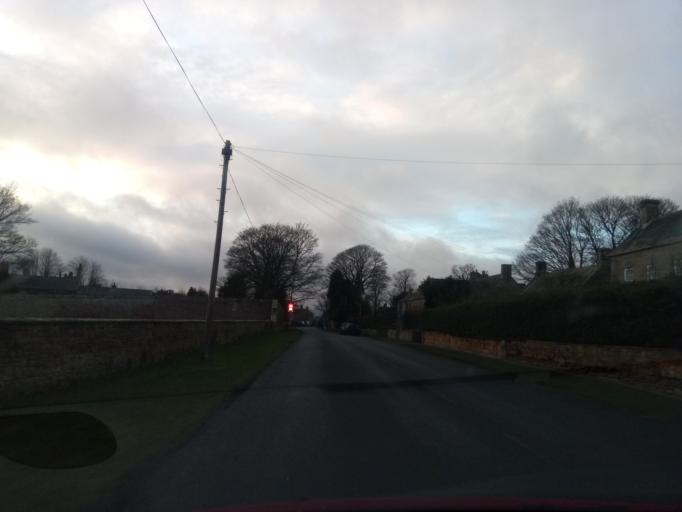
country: GB
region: England
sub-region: Northumberland
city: Meldon
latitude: 55.1270
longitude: -1.7941
